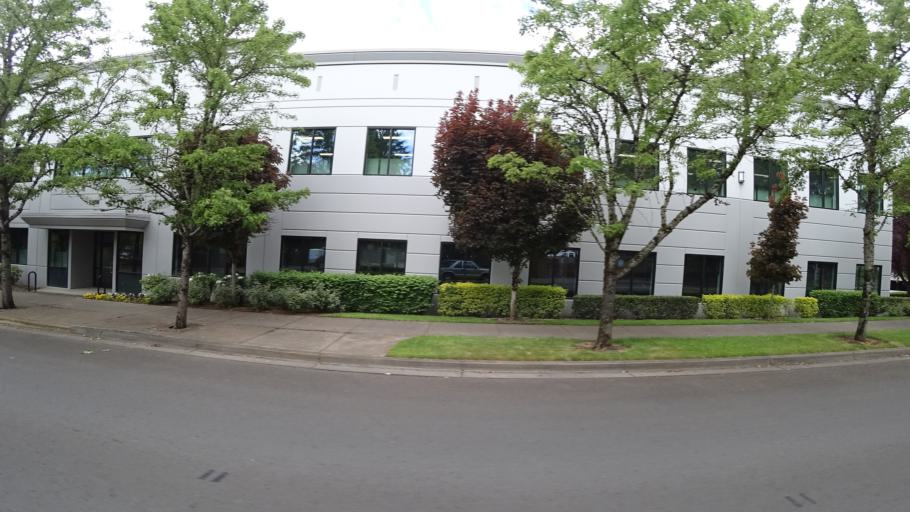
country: US
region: Oregon
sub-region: Washington County
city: Metzger
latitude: 45.4311
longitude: -122.7479
